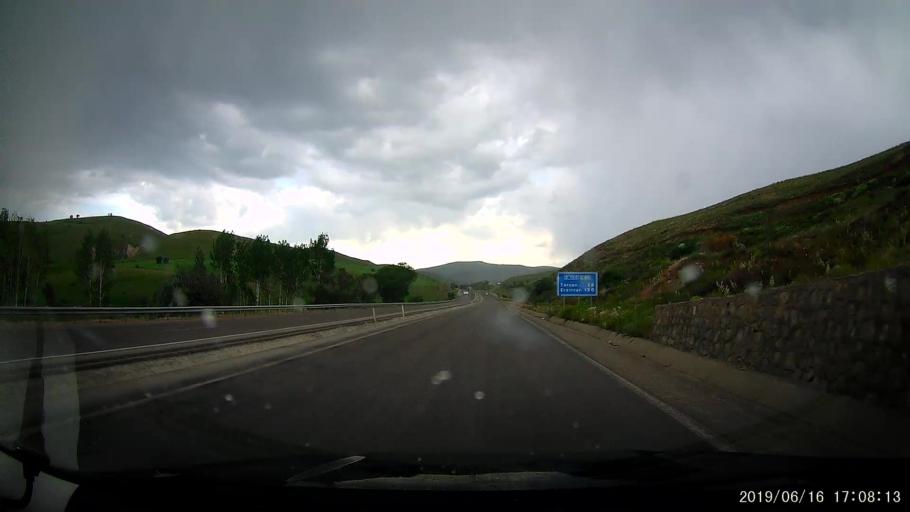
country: TR
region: Erzurum
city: Askale
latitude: 39.9122
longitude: 40.6637
